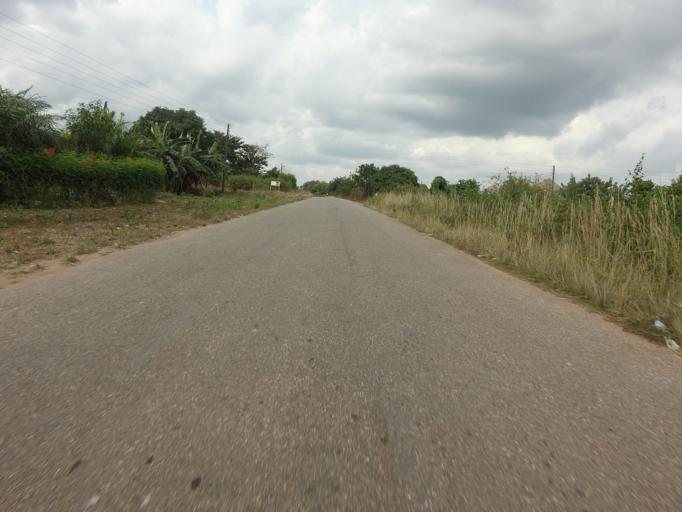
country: GH
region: Volta
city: Ho
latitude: 6.6650
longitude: 0.3507
